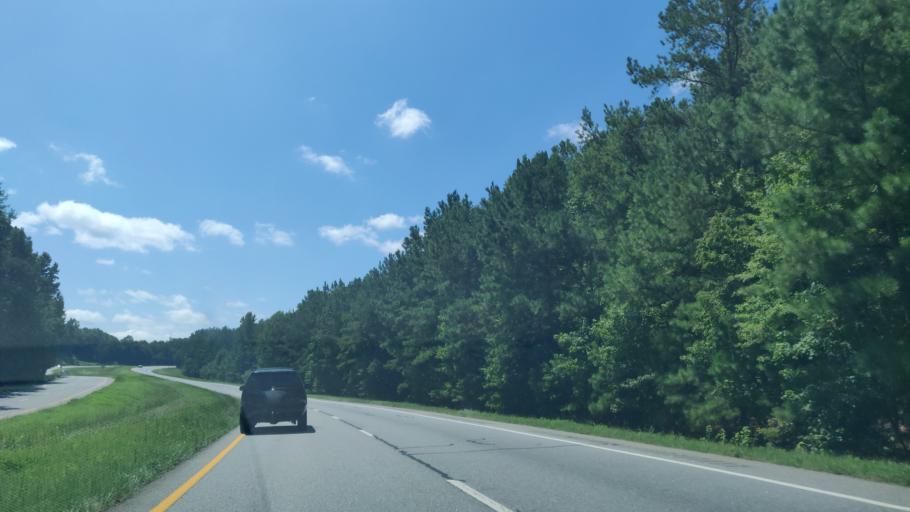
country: US
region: Georgia
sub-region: Chattahoochee County
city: Cusseta
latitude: 32.2435
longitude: -84.7181
